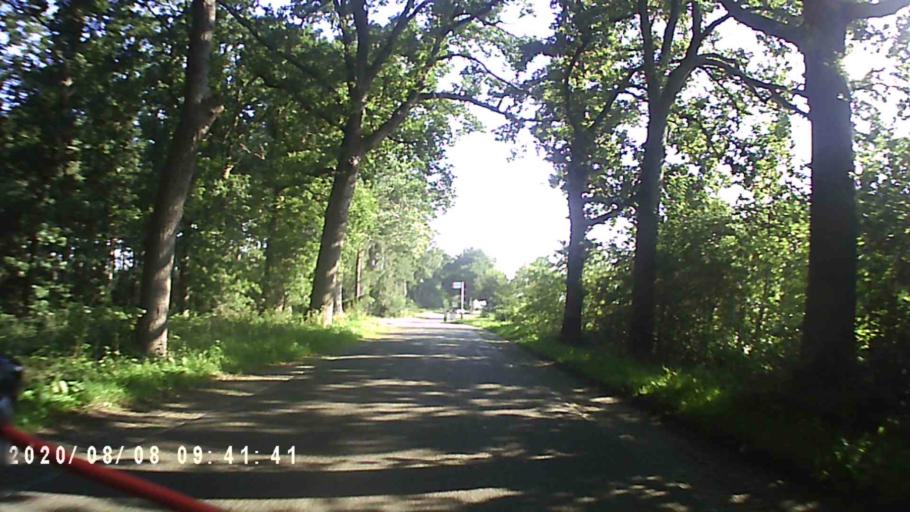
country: NL
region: Groningen
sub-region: Gemeente Leek
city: Leek
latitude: 53.0659
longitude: 6.4002
